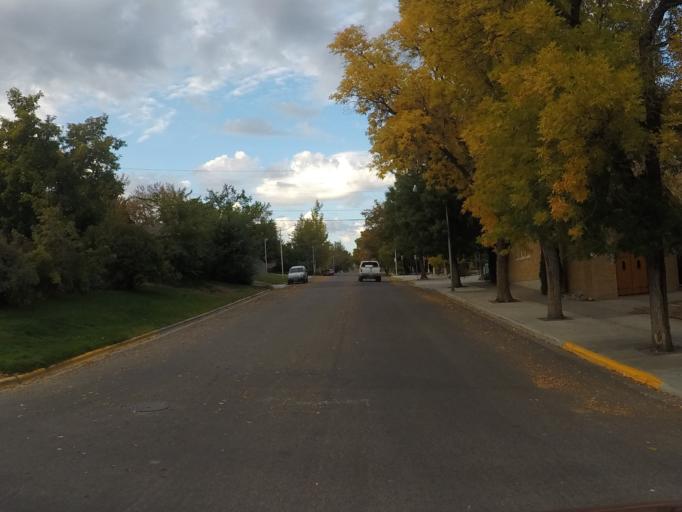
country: US
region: Montana
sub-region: Yellowstone County
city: Billings
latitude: 45.7841
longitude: -108.5306
